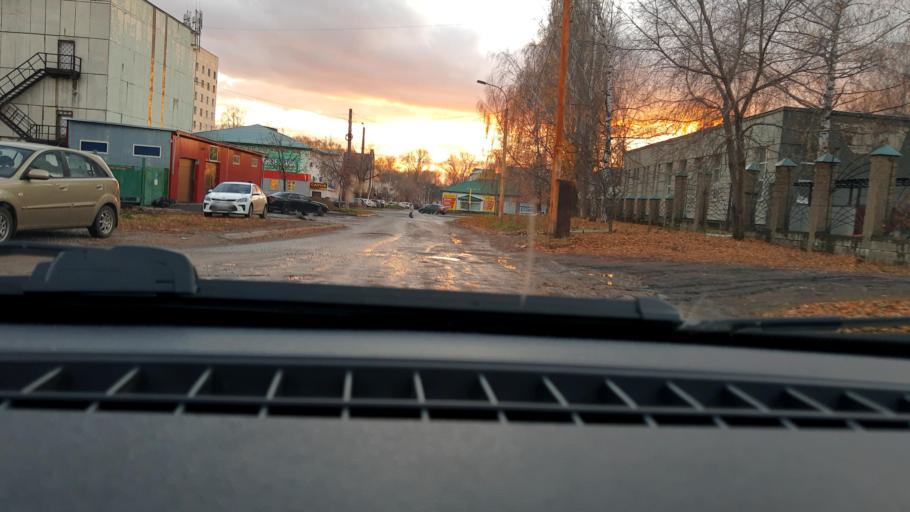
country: RU
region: Bashkortostan
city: Ufa
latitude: 54.8236
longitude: 56.1034
